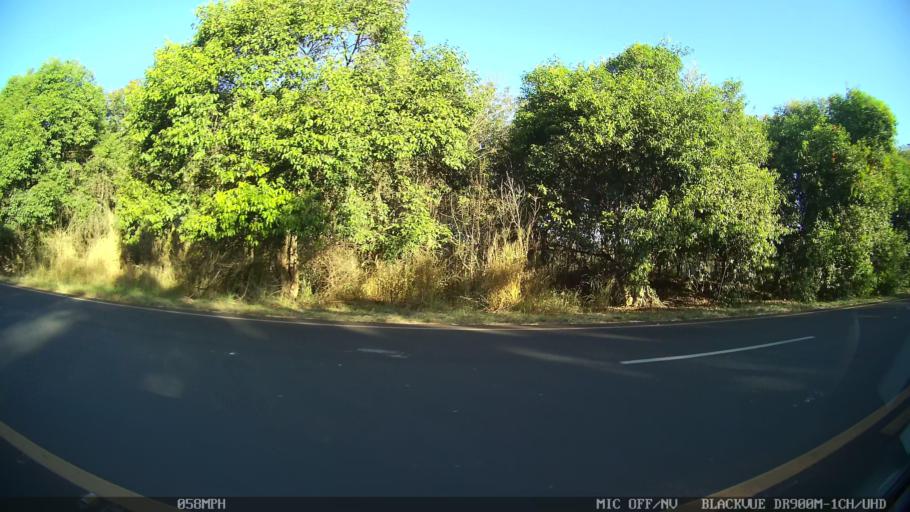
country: BR
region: Sao Paulo
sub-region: Guapiacu
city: Guapiacu
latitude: -20.7627
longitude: -49.1838
